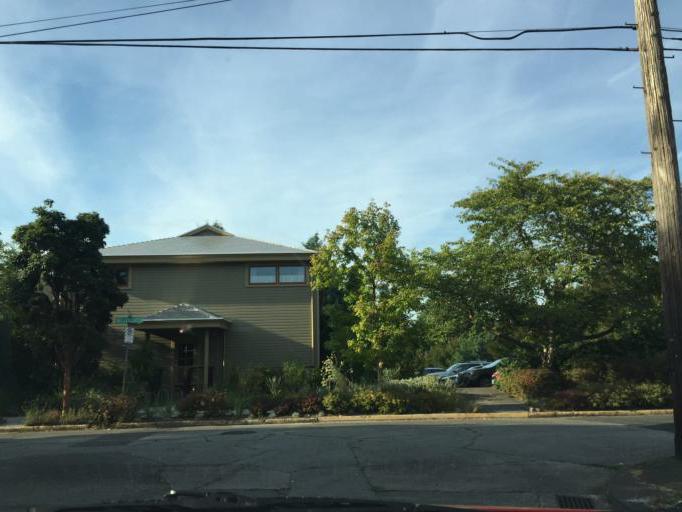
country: US
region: Oregon
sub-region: Multnomah County
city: Portland
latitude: 45.5637
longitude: -122.6296
